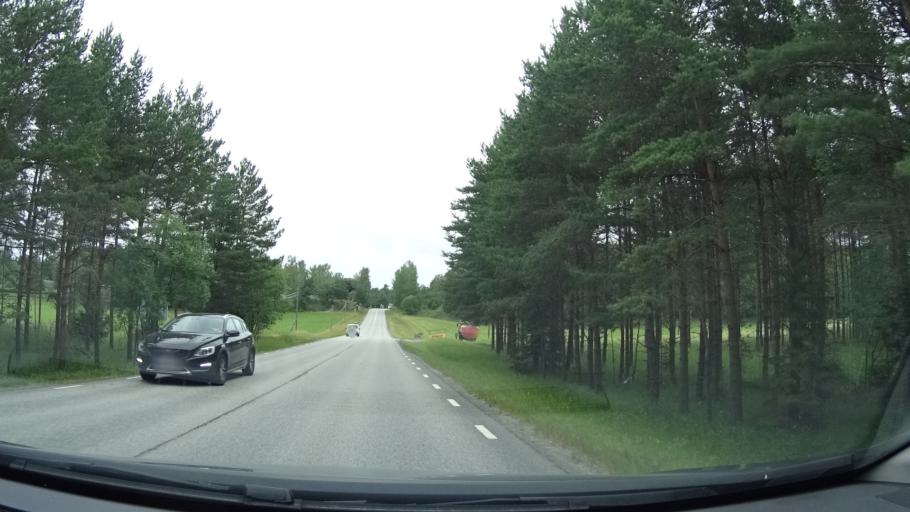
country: SE
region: Stockholm
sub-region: Varmdo Kommun
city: Hemmesta
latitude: 59.3481
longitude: 18.4789
